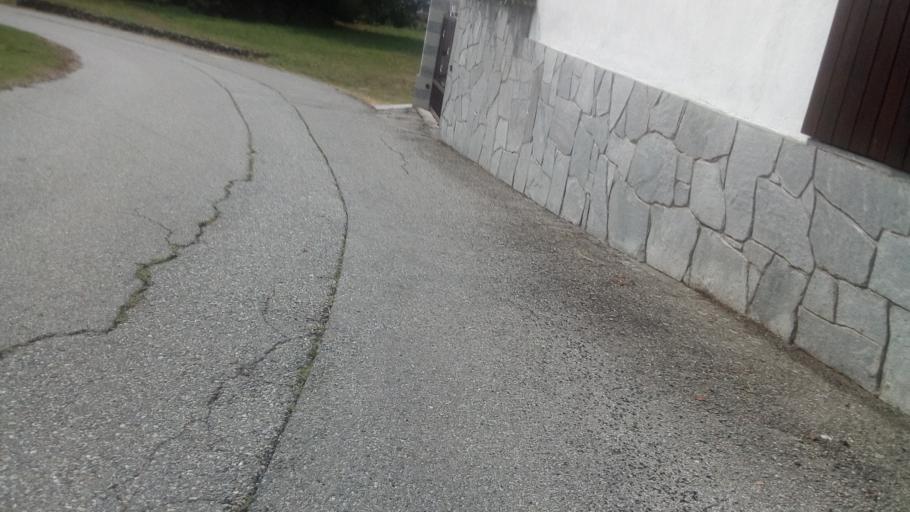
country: IT
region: Piedmont
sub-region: Provincia di Torino
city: Colleretto Giacosa
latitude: 45.4370
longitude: 7.7934
